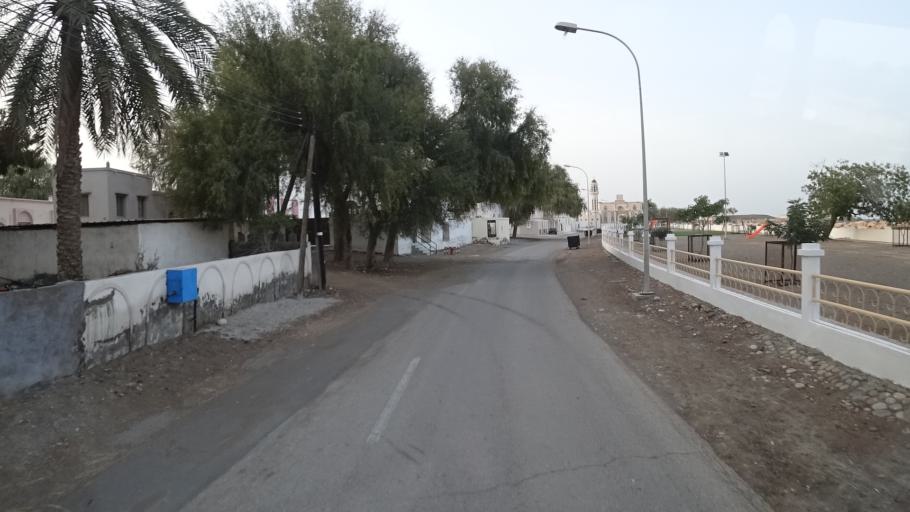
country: OM
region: Muhafazat Masqat
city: Muscat
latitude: 23.2140
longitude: 58.9737
